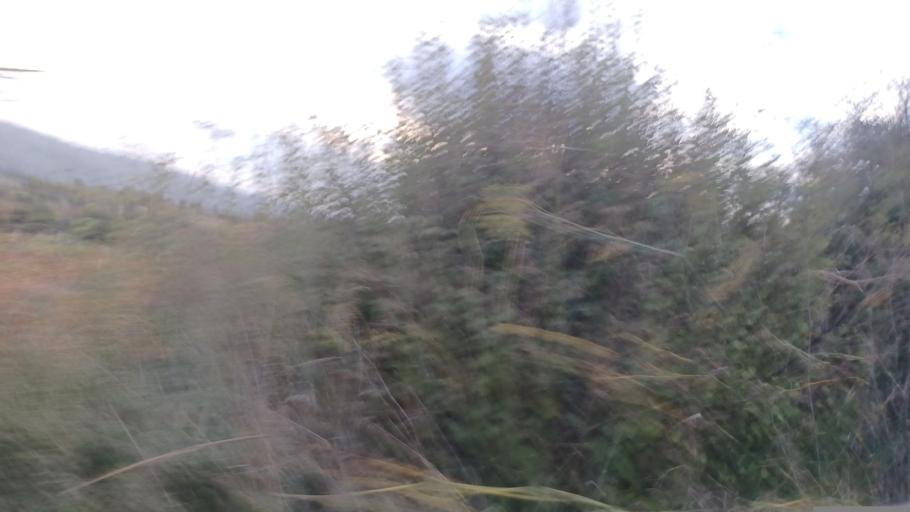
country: CY
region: Pafos
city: Mesogi
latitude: 34.8708
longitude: 32.5115
